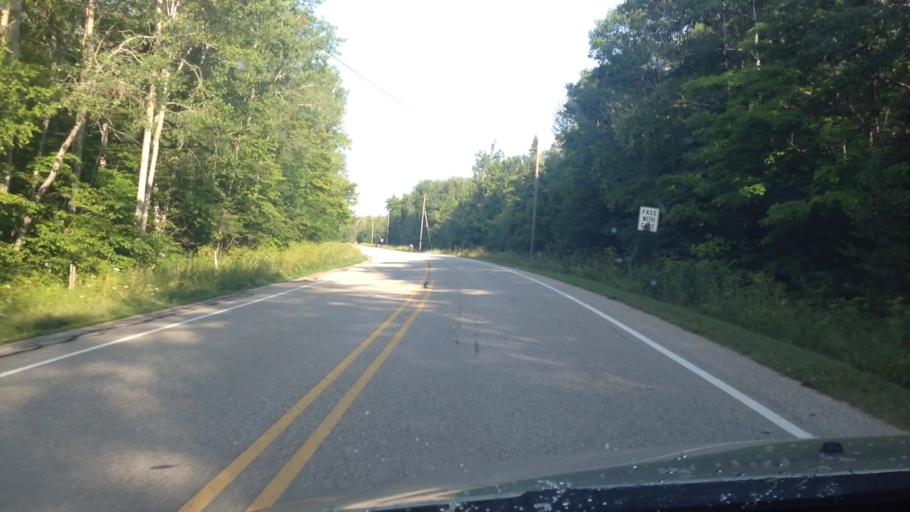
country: US
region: Michigan
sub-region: Mackinac County
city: Saint Ignace
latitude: 45.8924
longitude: -84.7961
